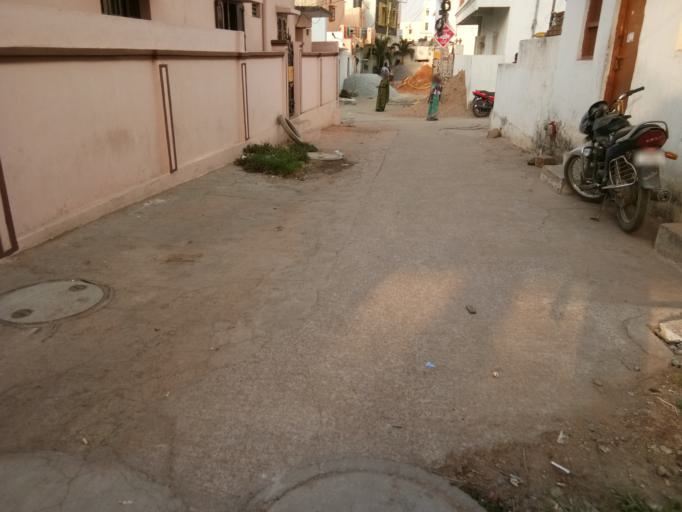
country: IN
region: Telangana
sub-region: Hyderabad
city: Hyderabad
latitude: 17.3254
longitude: 78.4257
